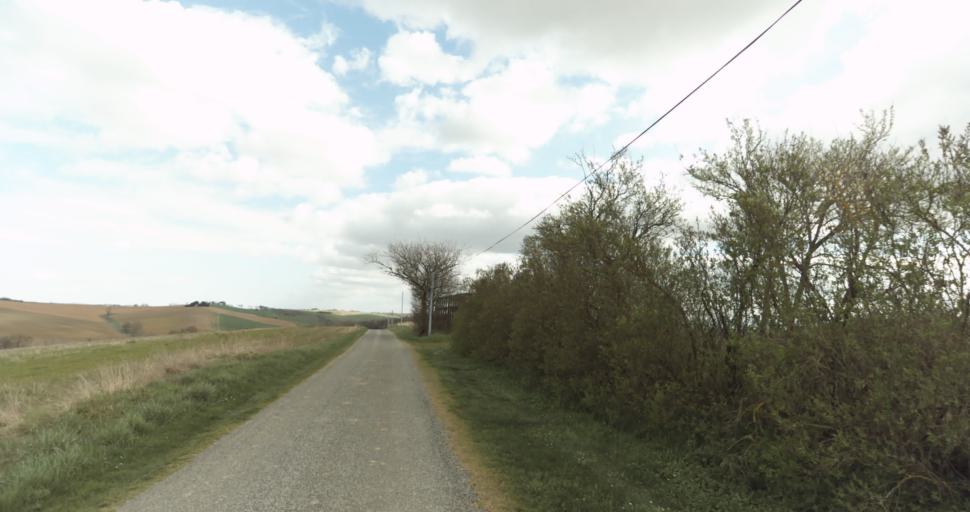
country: FR
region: Midi-Pyrenees
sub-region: Departement de la Haute-Garonne
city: Auterive
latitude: 43.3642
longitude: 1.4920
